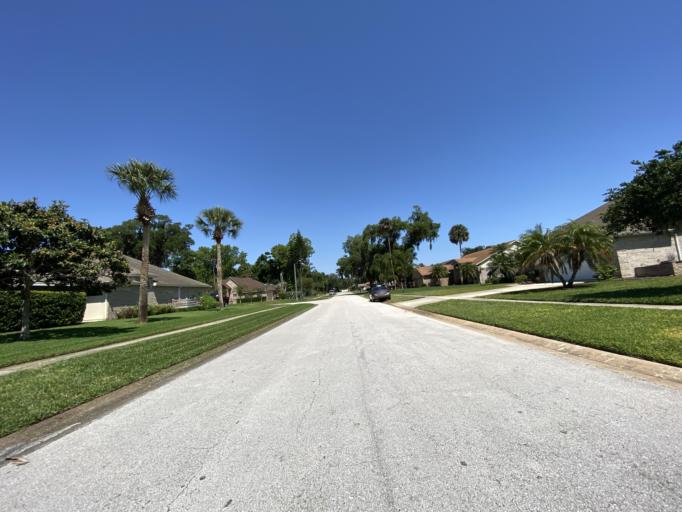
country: US
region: Florida
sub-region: Volusia County
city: South Daytona
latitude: 29.1548
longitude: -81.0111
